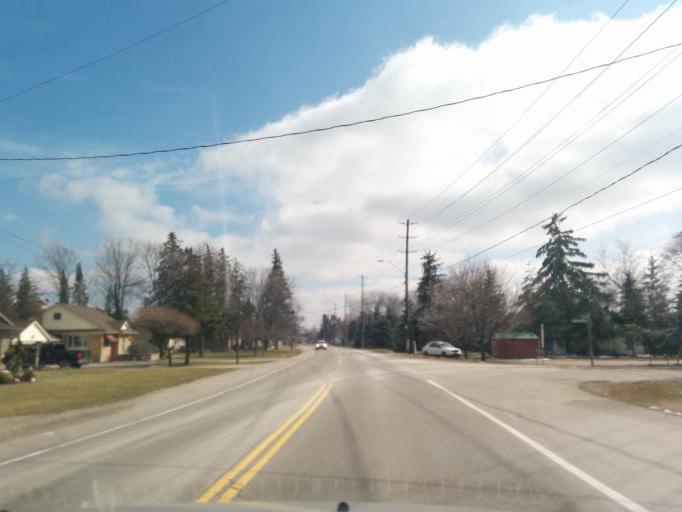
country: CA
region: Ontario
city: Waterloo
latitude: 43.5116
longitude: -80.4633
